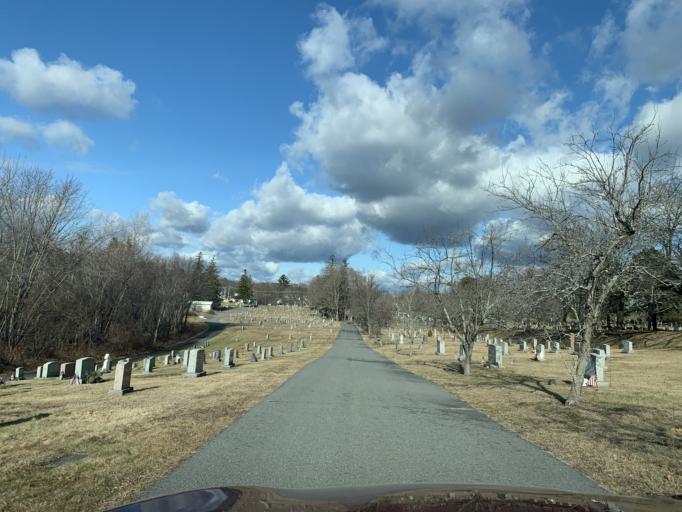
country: US
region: Massachusetts
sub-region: Essex County
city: Amesbury
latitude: 42.8424
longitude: -70.9339
